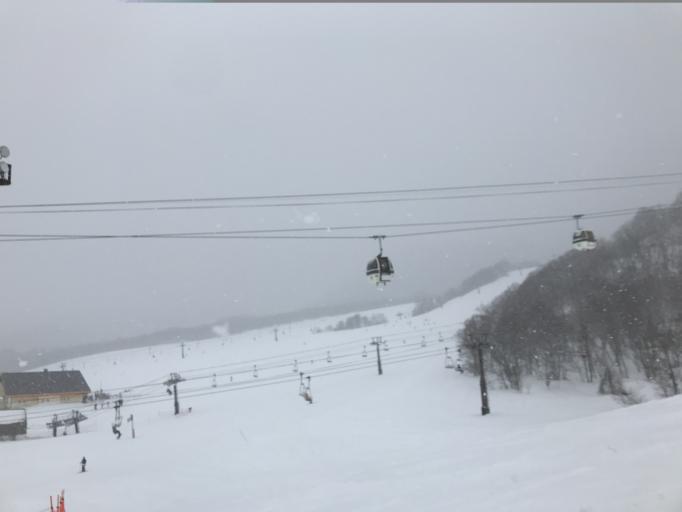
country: JP
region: Nagano
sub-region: Kitaazumi Gun
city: Hakuba
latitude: 36.7550
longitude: 137.8597
